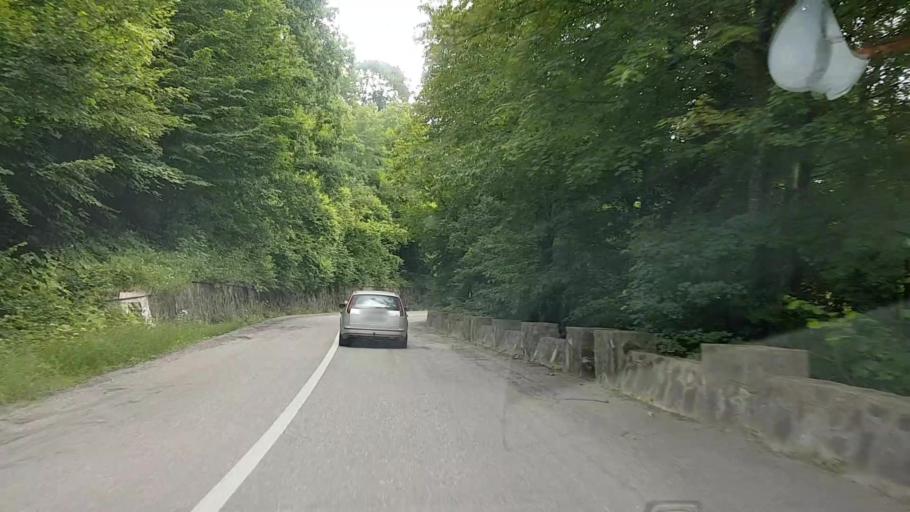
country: RO
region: Neamt
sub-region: Comuna Pangarati
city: Pangarati
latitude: 46.9440
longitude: 26.1258
